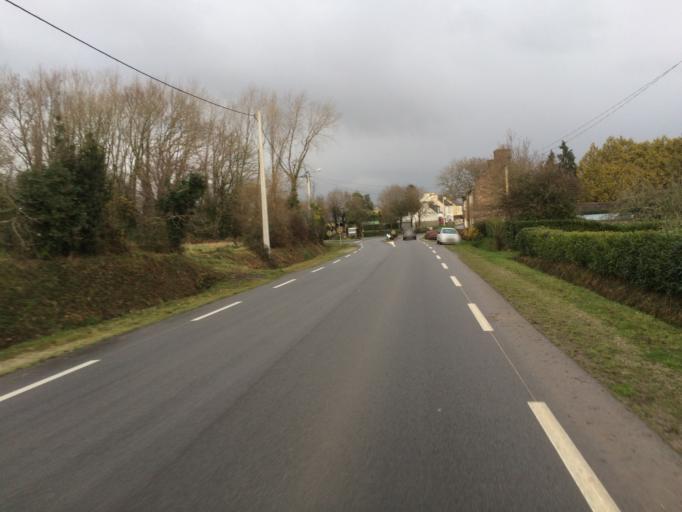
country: FR
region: Brittany
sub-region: Departement du Finistere
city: Logonna-Daoulas
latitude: 48.3338
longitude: -4.2887
